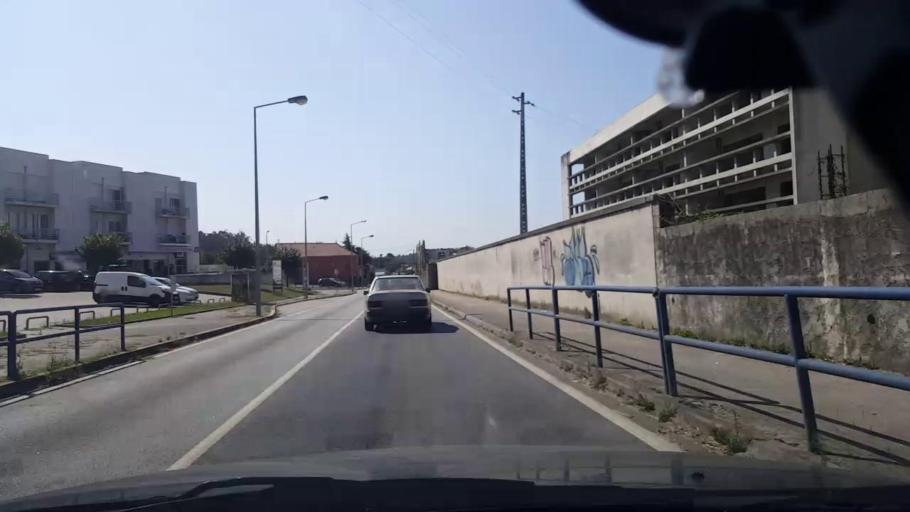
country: PT
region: Porto
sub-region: Povoa de Varzim
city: Pedroso
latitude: 41.4010
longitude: -8.6829
